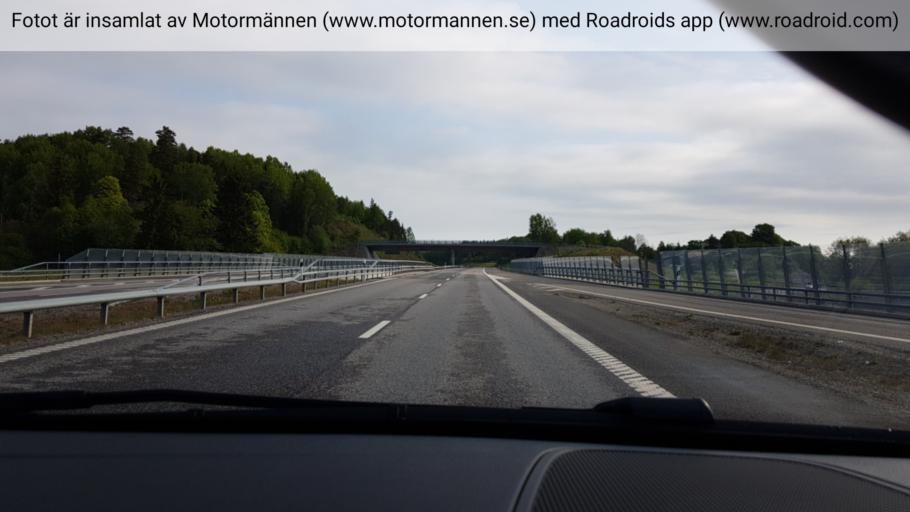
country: SE
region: Stockholm
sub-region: Nynashamns Kommun
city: Osmo
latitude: 58.9962
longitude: 17.9330
